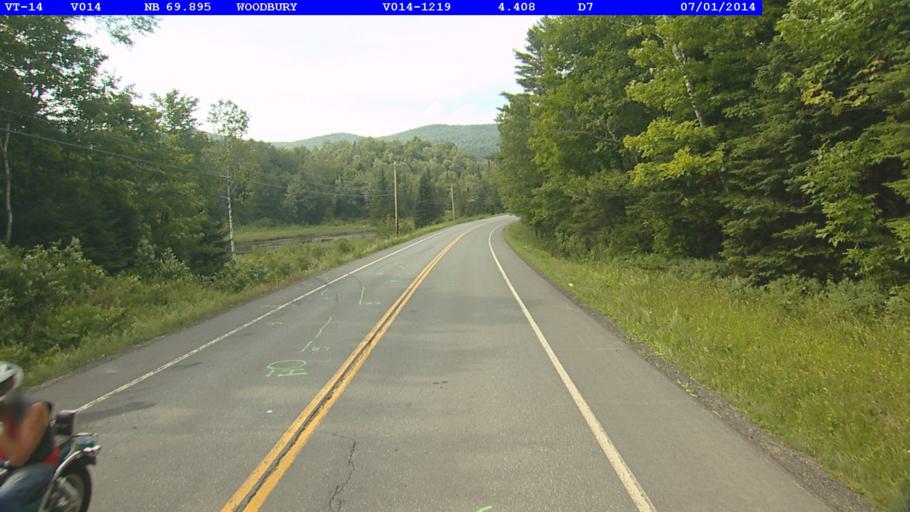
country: US
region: Vermont
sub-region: Caledonia County
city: Hardwick
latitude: 44.4510
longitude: -72.4189
